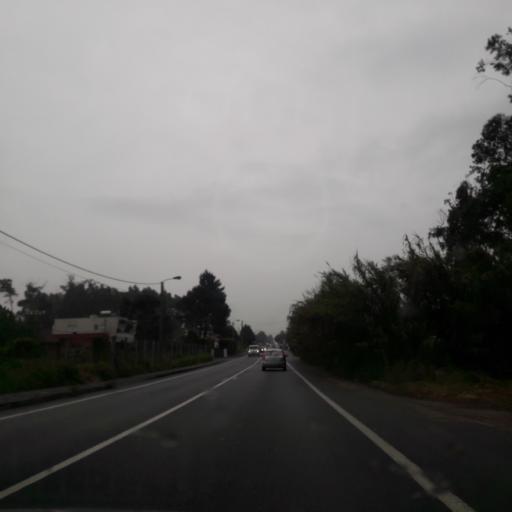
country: PT
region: Porto
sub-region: Vila do Conde
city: Arvore
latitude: 41.3143
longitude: -8.7086
